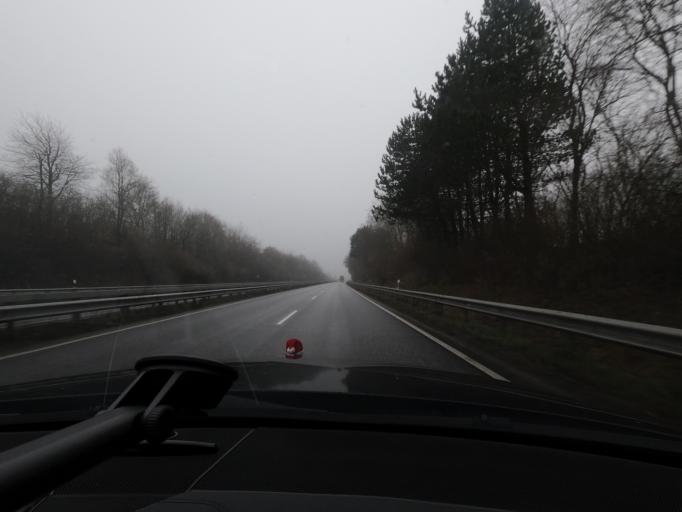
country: DE
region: Schleswig-Holstein
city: Jarplund-Weding
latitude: 54.7416
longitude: 9.4119
